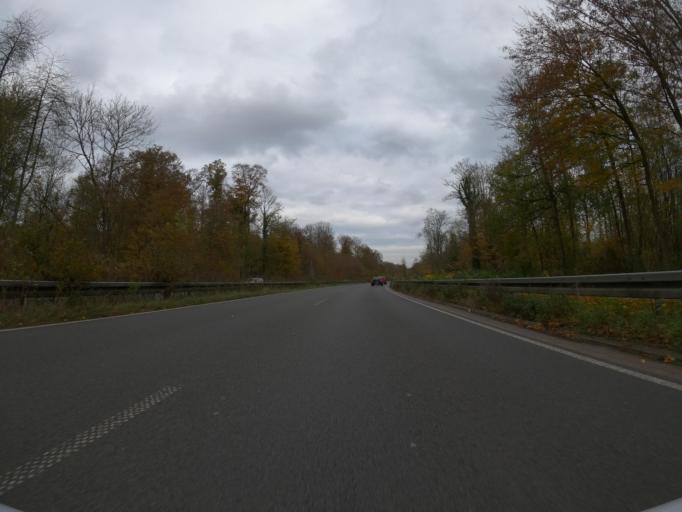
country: DE
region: North Rhine-Westphalia
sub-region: Regierungsbezirk Dusseldorf
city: Essen
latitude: 51.4206
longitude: 7.0590
